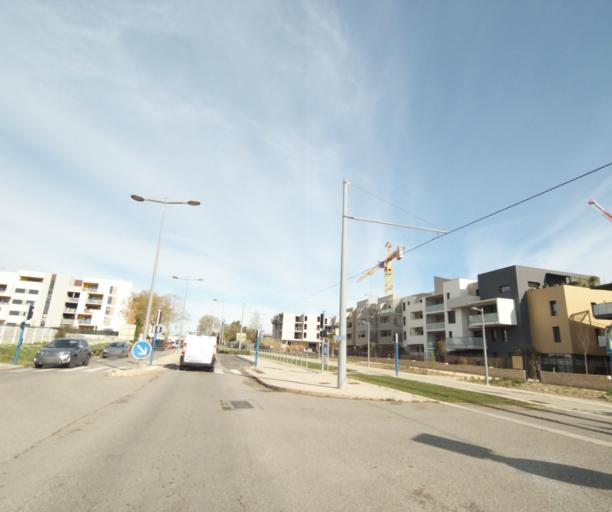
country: FR
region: Languedoc-Roussillon
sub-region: Departement de l'Herault
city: Saint-Jean-de-Vedas
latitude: 43.5736
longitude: 3.8329
